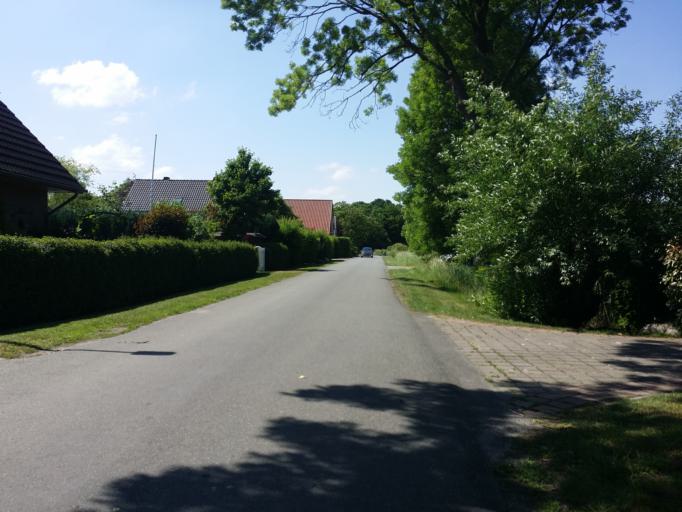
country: DE
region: Lower Saxony
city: Lemwerder
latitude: 53.1424
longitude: 8.5722
